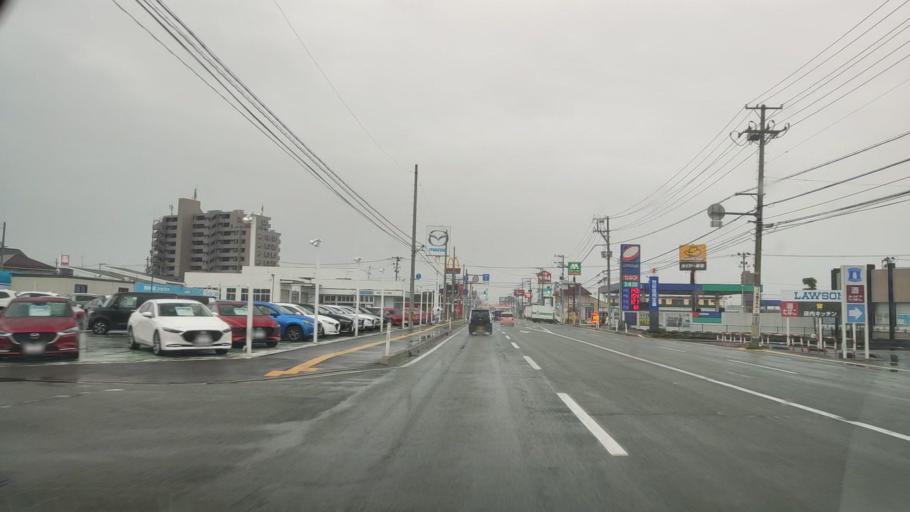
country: JP
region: Akita
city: Akita Shi
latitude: 39.7349
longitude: 140.0995
